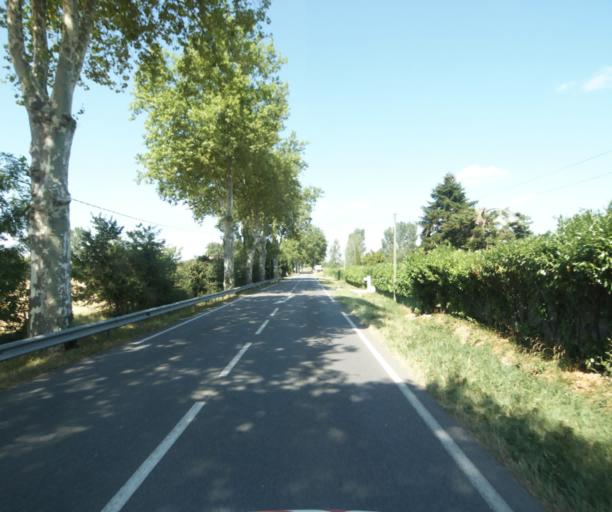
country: FR
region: Midi-Pyrenees
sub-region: Departement de la Haute-Garonne
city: Revel
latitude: 43.4721
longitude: 2.0135
